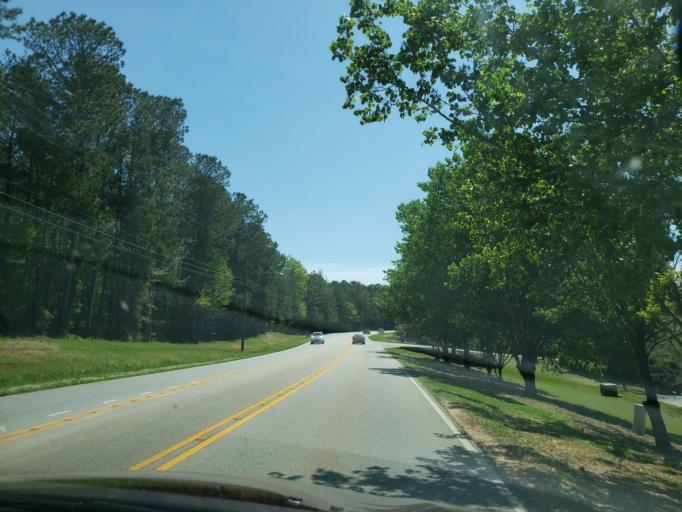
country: US
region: Alabama
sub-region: Lee County
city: Auburn
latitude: 32.6333
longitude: -85.5000
